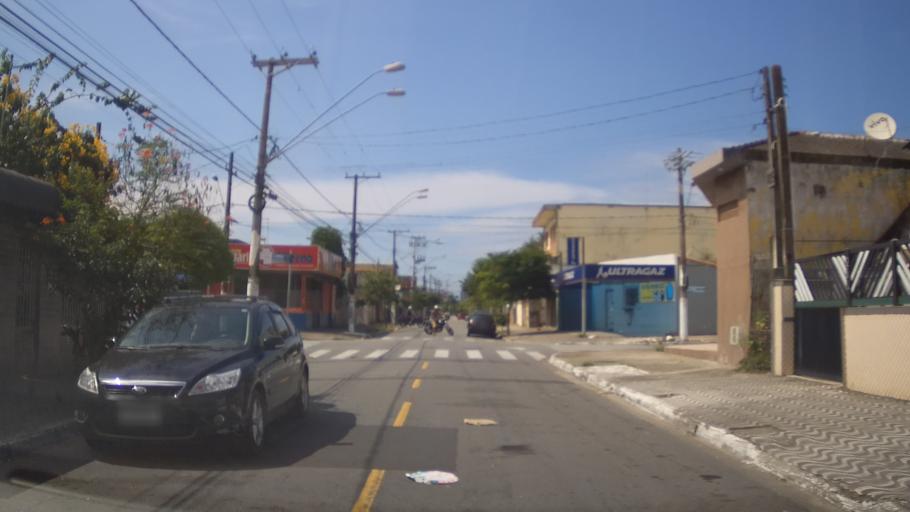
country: BR
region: Sao Paulo
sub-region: Praia Grande
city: Praia Grande
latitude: -24.0202
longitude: -46.4855
